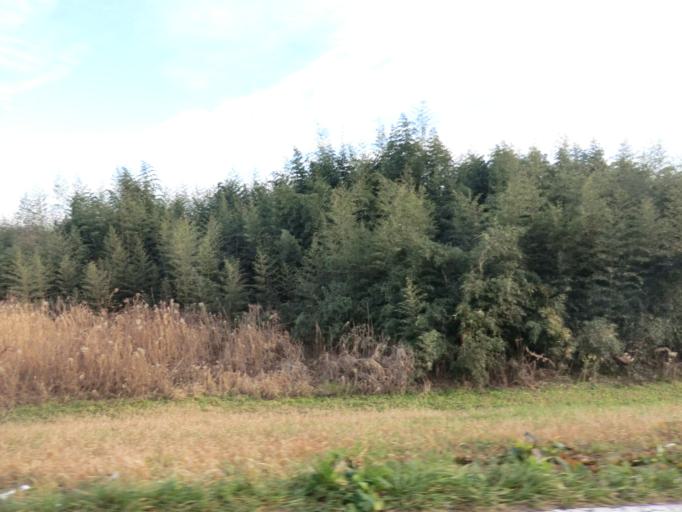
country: JP
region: Ibaraki
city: Mitsukaido
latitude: 36.0319
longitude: 140.0258
